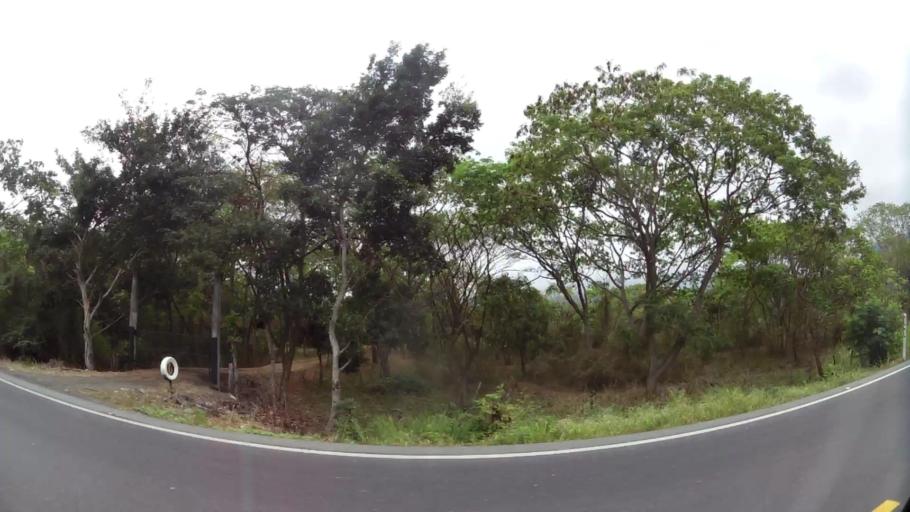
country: EC
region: Guayas
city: Naranjal
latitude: -2.4230
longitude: -79.6251
